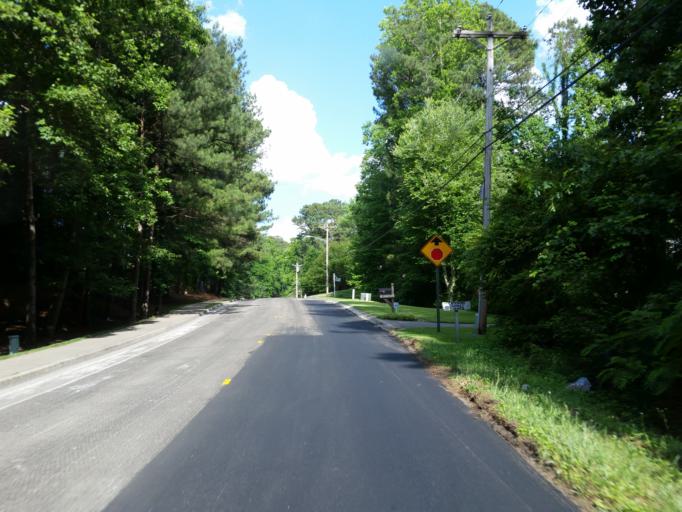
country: US
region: Georgia
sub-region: Fulton County
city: Roswell
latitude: 34.0045
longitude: -84.4243
